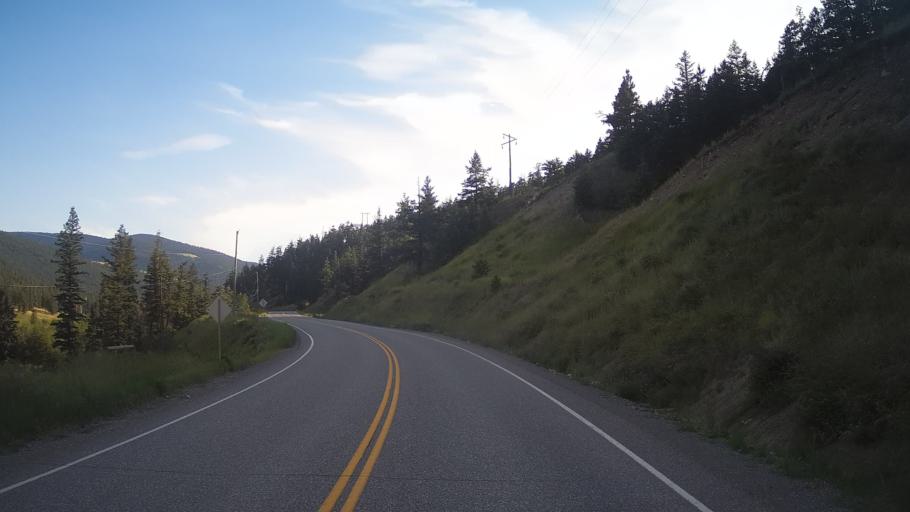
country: CA
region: British Columbia
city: Cache Creek
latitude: 50.8618
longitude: -121.5289
